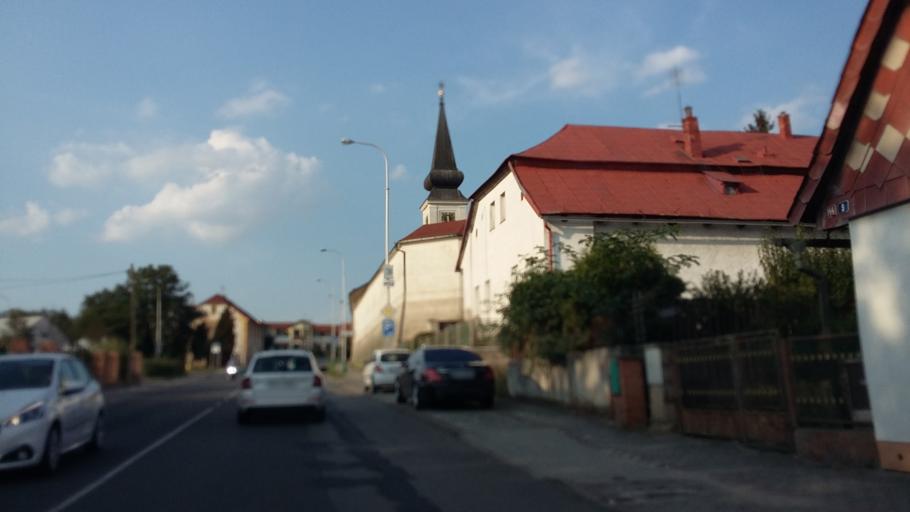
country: CZ
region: Central Bohemia
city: Kosmonosy
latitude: 50.4378
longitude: 14.9295
